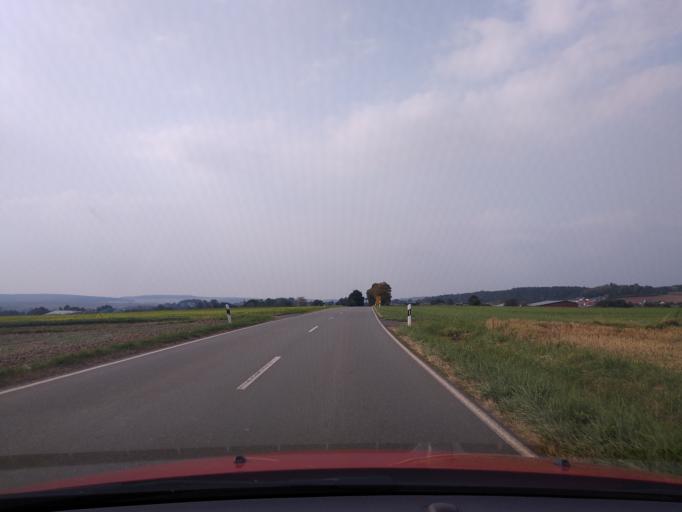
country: DE
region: Hesse
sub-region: Regierungsbezirk Kassel
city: Zierenberg
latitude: 51.4265
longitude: 9.3338
